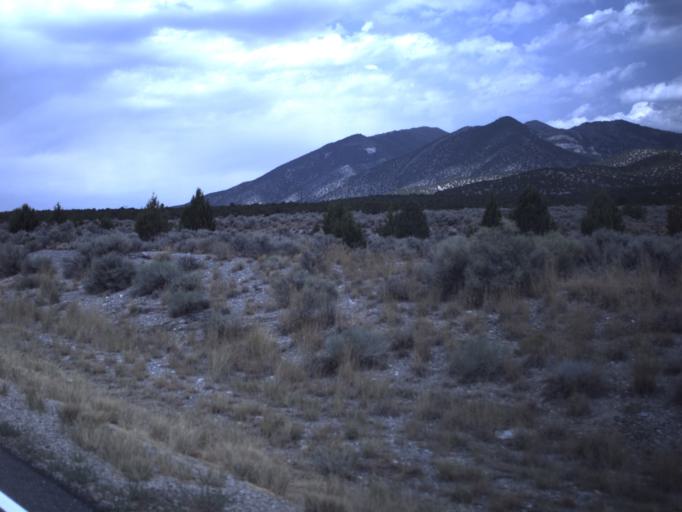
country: US
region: Utah
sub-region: Tooele County
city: Tooele
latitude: 40.3274
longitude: -112.2903
